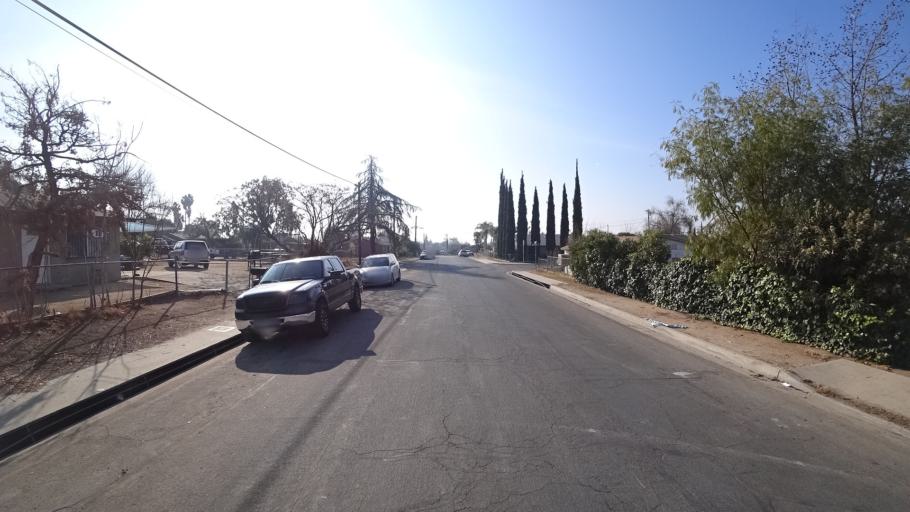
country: US
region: California
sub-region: Kern County
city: Bakersfield
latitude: 35.3951
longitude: -118.9808
